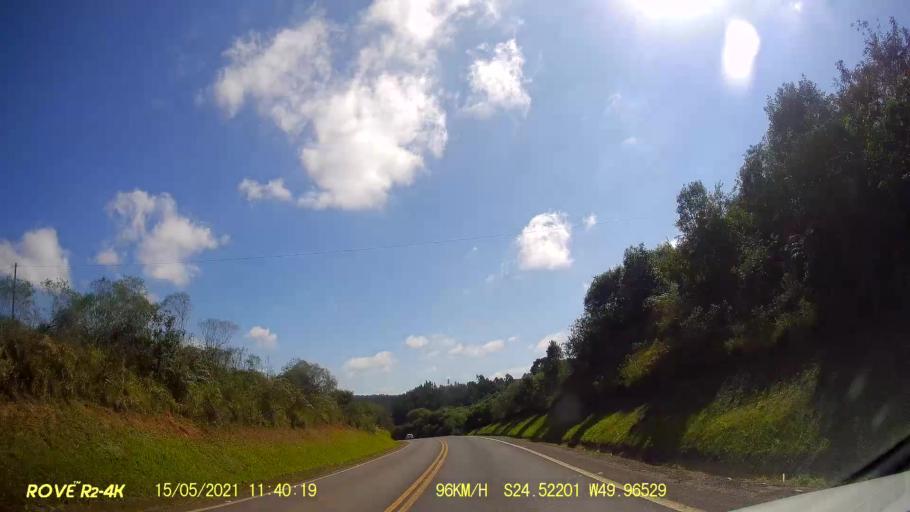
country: BR
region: Parana
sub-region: Pirai Do Sul
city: Pirai do Sul
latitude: -24.5222
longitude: -49.9653
